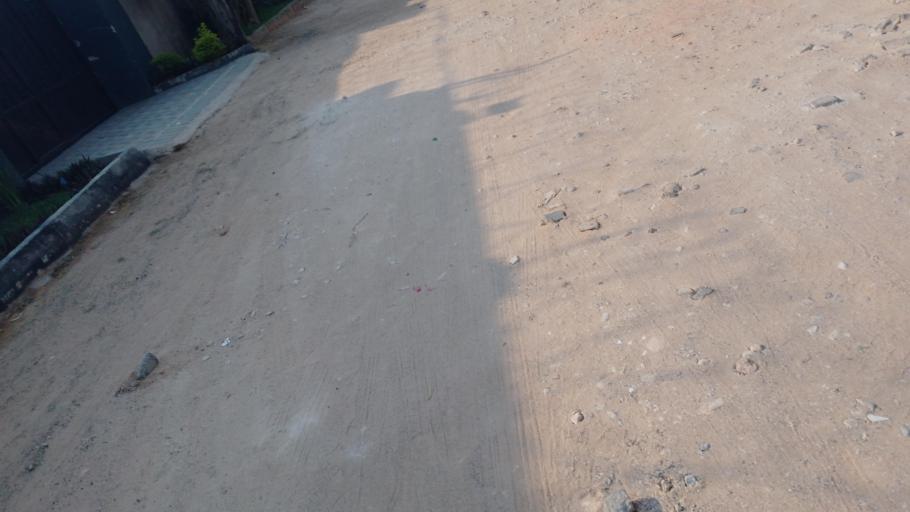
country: ZM
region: Lusaka
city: Lusaka
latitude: -15.3987
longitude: 28.3873
